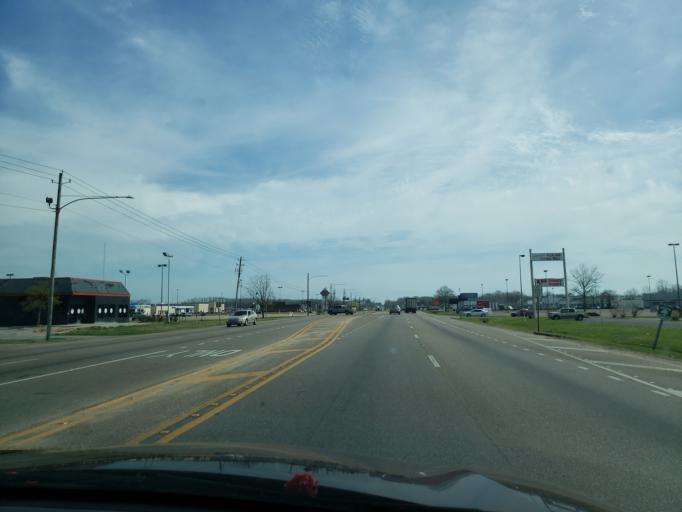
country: US
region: Alabama
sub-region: Dallas County
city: Selma
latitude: 32.4314
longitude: -87.0197
